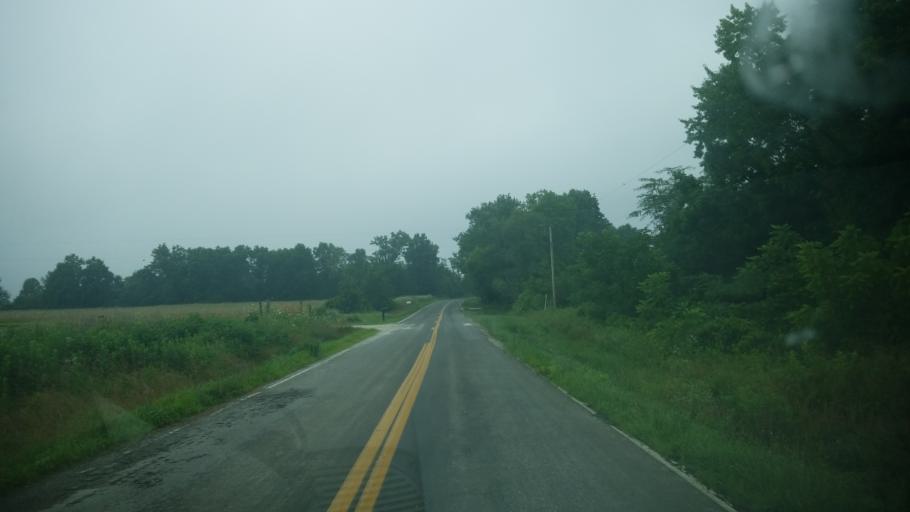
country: US
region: Missouri
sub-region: Audrain County
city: Vandalia
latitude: 39.2967
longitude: -91.3508
